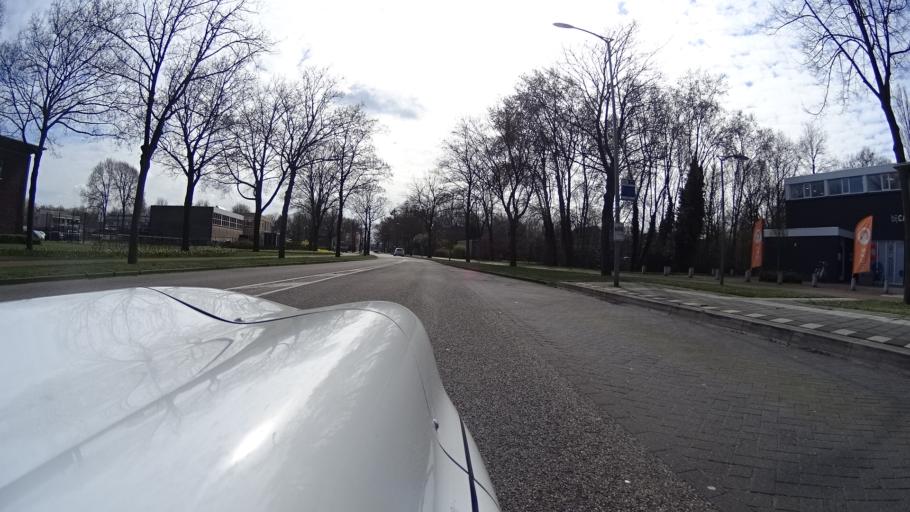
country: NL
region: North Brabant
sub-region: Gemeente 's-Hertogenbosch
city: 's-Hertogenbosch
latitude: 51.7081
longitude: 5.3617
